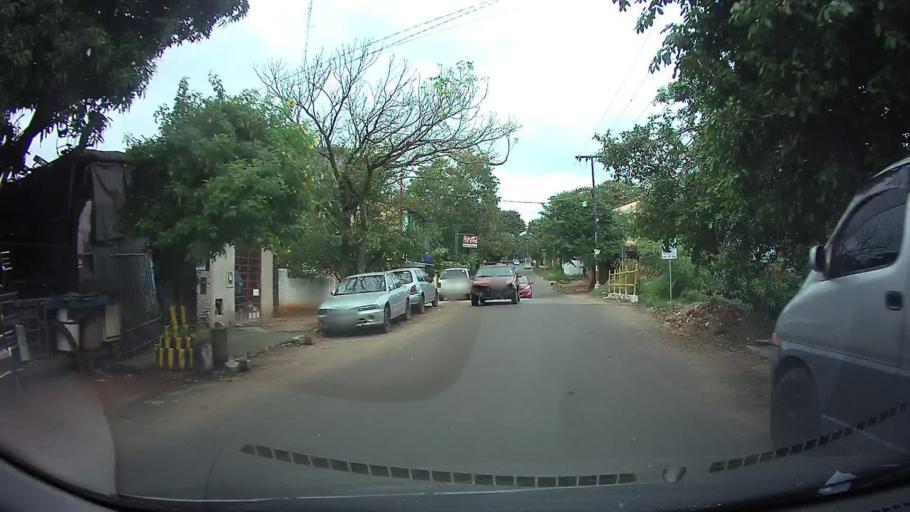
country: PY
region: Central
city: Lambare
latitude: -25.3199
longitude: -57.6134
